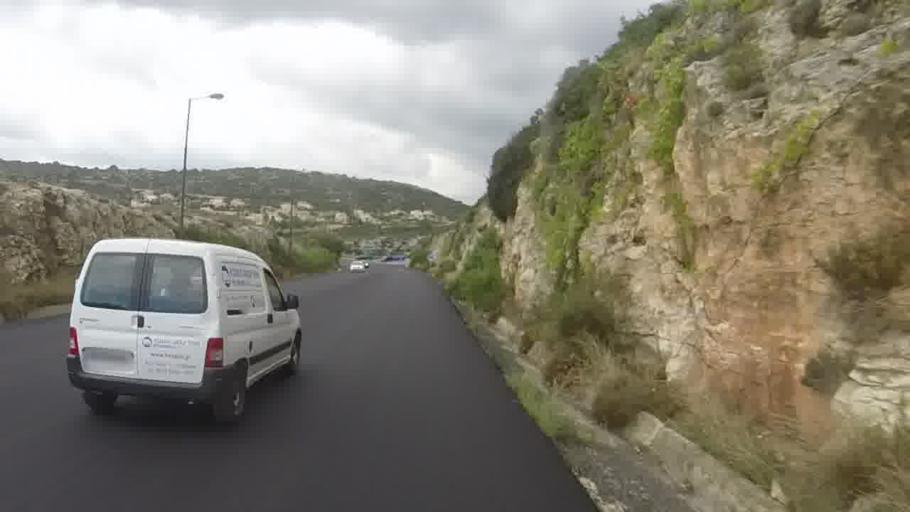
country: GR
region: Crete
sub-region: Nomos Rethymnis
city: Atsipopoulon
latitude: 35.3607
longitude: 24.4055
